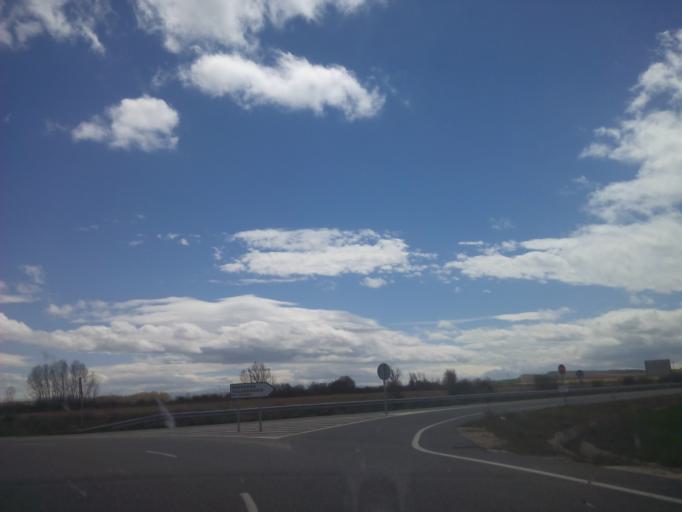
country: ES
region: Castille and Leon
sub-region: Provincia de Salamanca
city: Machacon
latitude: 40.9209
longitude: -5.5070
